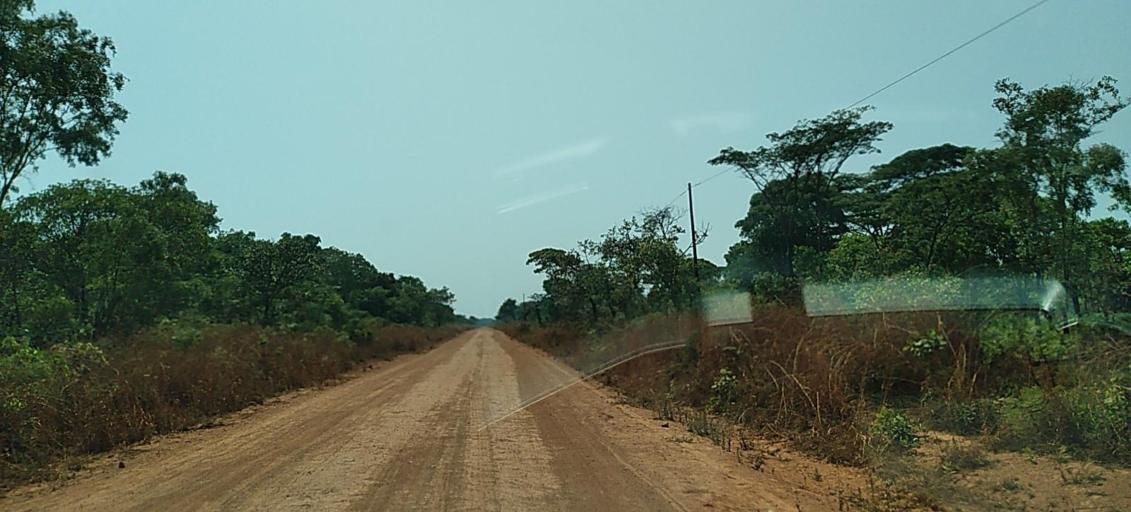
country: ZM
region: North-Western
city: Kansanshi
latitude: -11.9934
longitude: 26.6332
